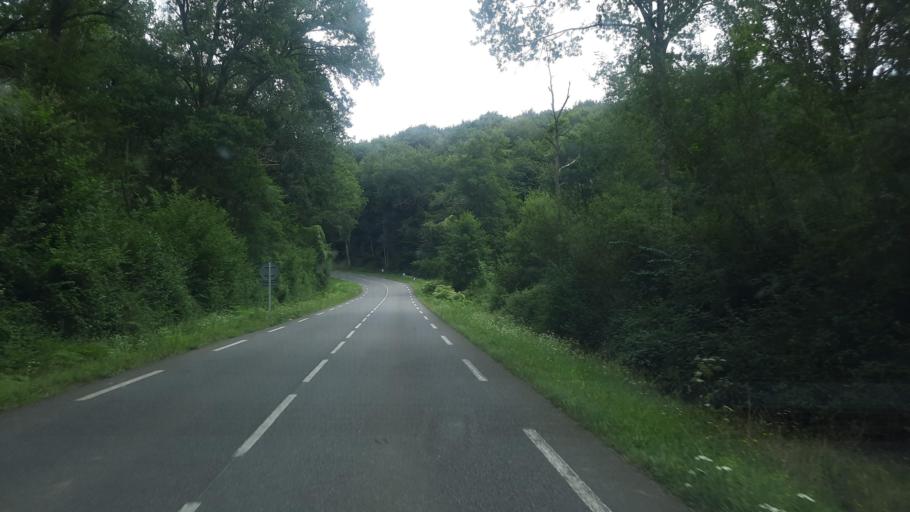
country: FR
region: Midi-Pyrenees
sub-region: Departement des Hautes-Pyrenees
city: Trie-sur-Baise
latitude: 43.2985
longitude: 0.4309
